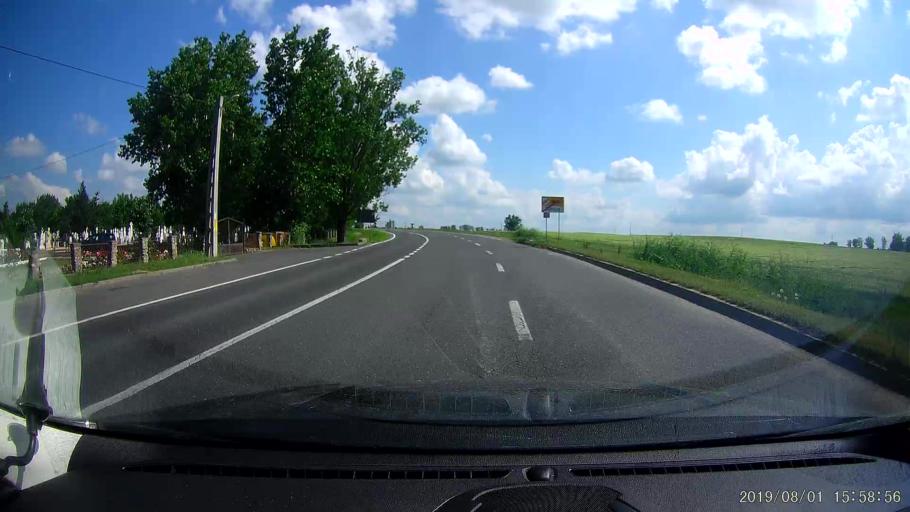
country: RO
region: Ialomita
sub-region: Comuna Slobozia
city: Slobozia
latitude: 44.5583
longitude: 27.3808
